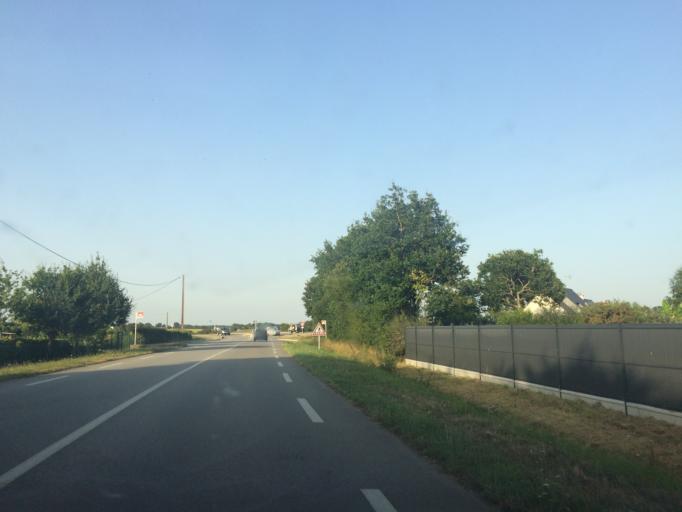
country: FR
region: Brittany
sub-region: Departement du Morbihan
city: Ambon
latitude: 47.5359
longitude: -2.5447
